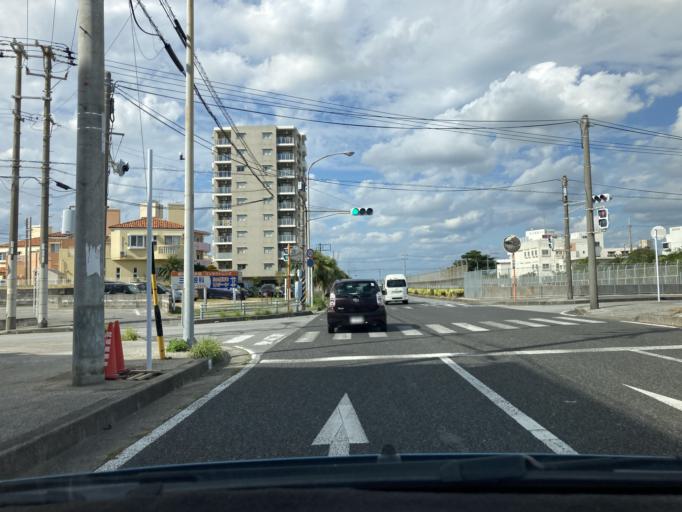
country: JP
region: Okinawa
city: Okinawa
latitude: 26.3249
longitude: 127.7874
